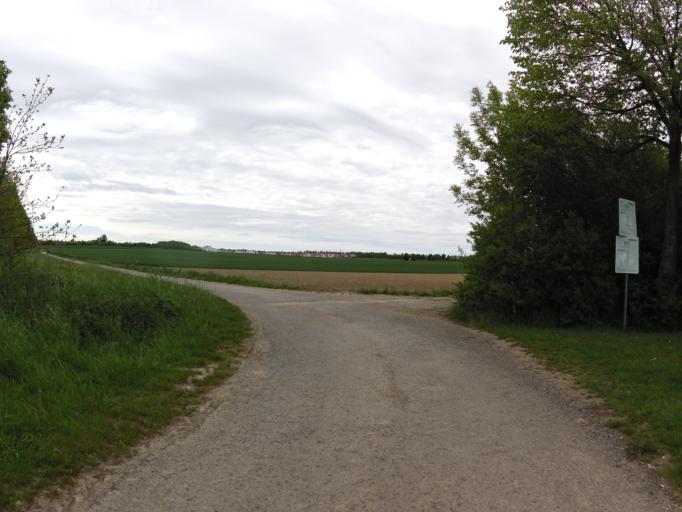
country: DE
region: Bavaria
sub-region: Regierungsbezirk Unterfranken
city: Unterpleichfeld
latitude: 49.8479
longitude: 10.0639
